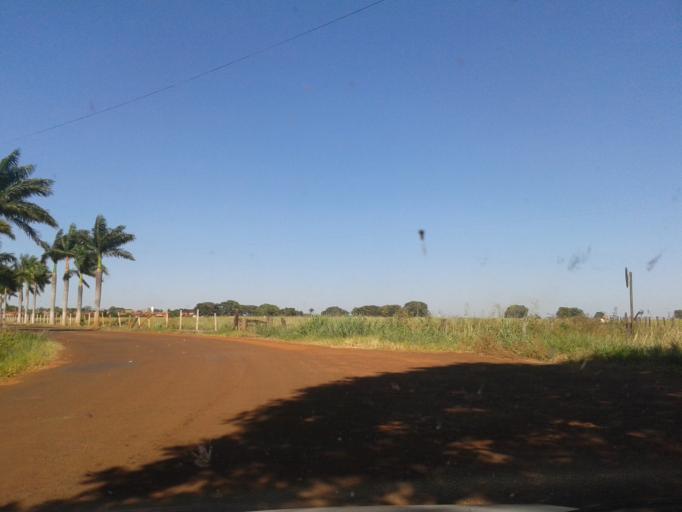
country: BR
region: Minas Gerais
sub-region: Santa Vitoria
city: Santa Vitoria
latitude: -18.6859
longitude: -49.9428
